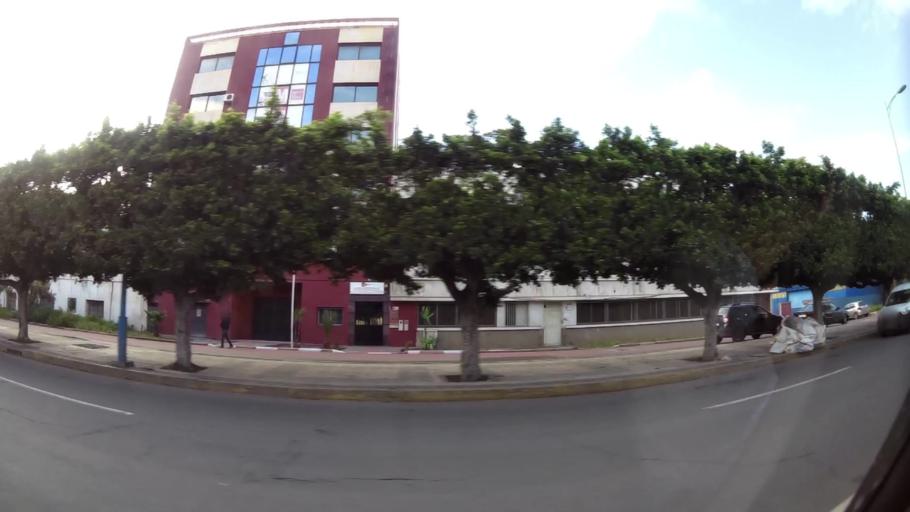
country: MA
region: Grand Casablanca
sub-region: Mohammedia
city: Mohammedia
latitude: 33.6888
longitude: -7.3979
